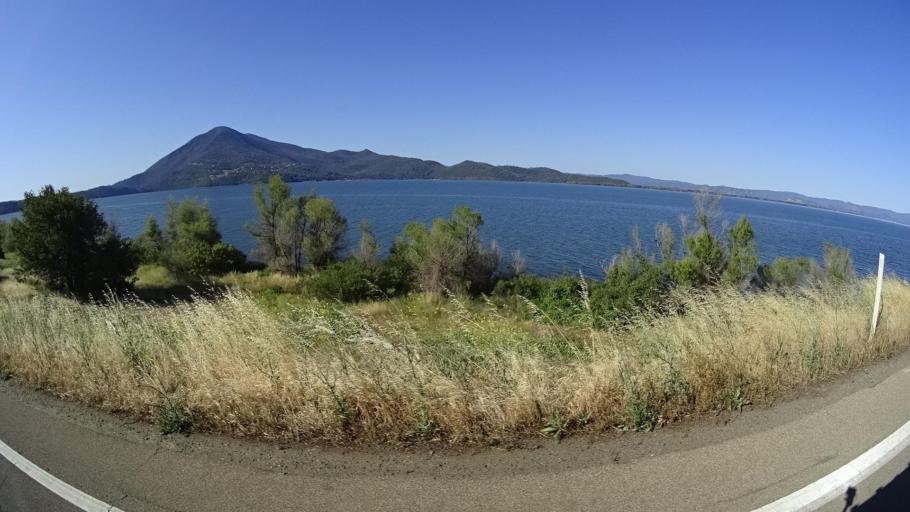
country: US
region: California
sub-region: Lake County
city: Soda Bay
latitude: 39.0441
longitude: -122.7777
